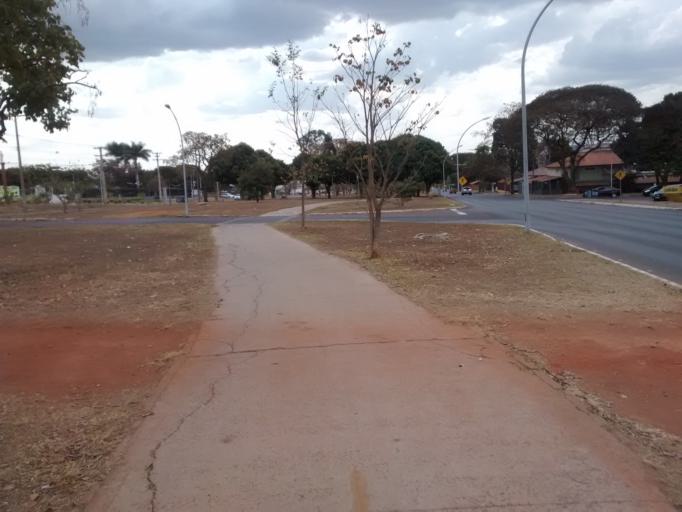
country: BR
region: Federal District
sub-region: Brasilia
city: Brasilia
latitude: -15.7459
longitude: -47.8999
